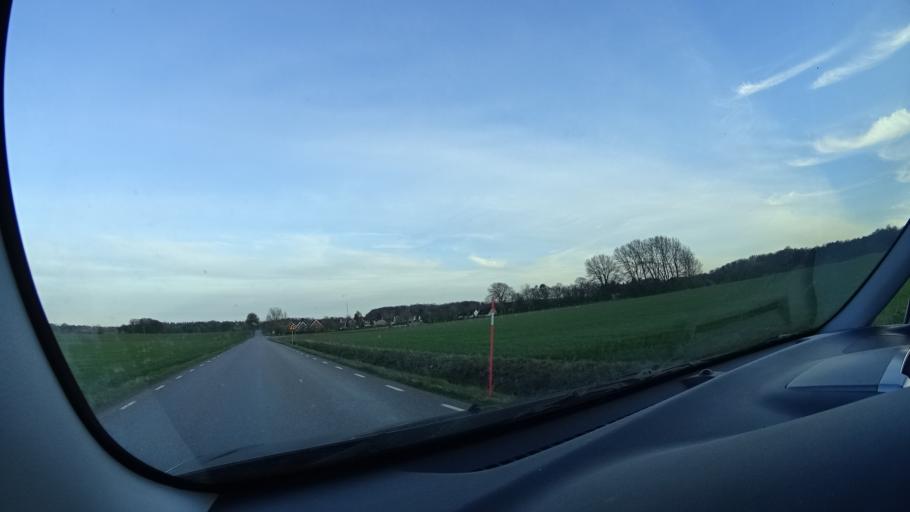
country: SE
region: Skane
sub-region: Eslovs Kommun
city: Stehag
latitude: 55.9089
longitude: 13.3932
